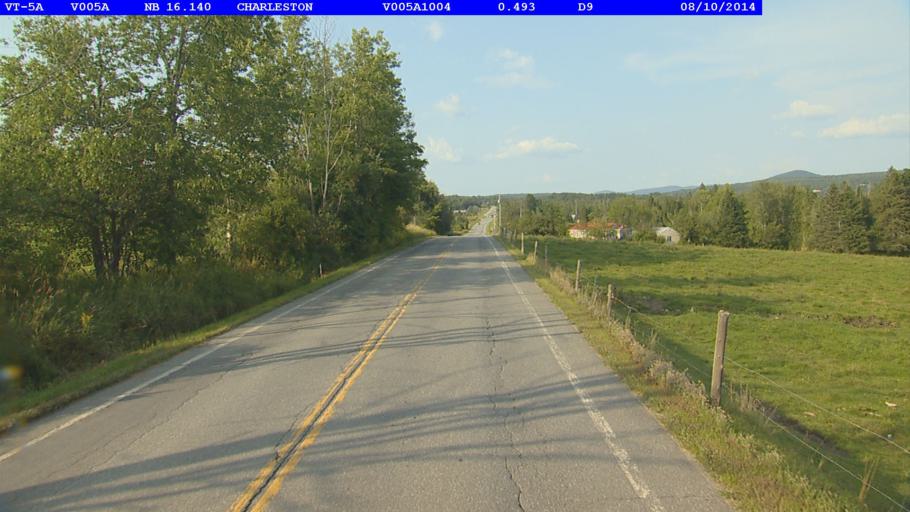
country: US
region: Vermont
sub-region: Orleans County
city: Newport
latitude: 44.8412
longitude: -72.0613
